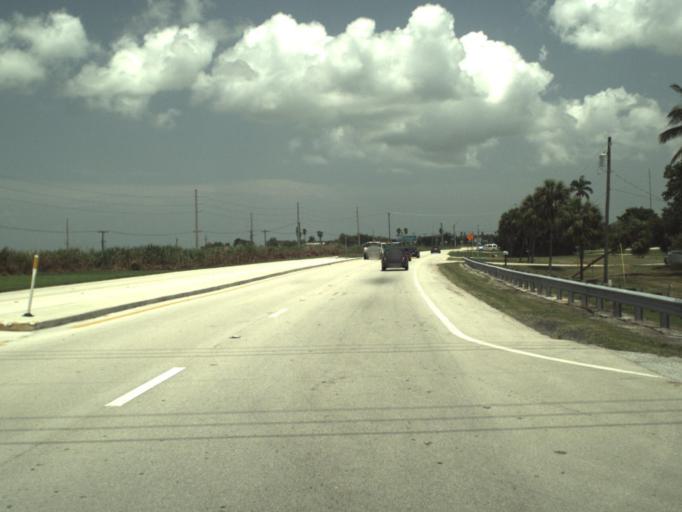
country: US
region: Florida
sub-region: Palm Beach County
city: Belle Glade
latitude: 26.7215
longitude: -80.6679
